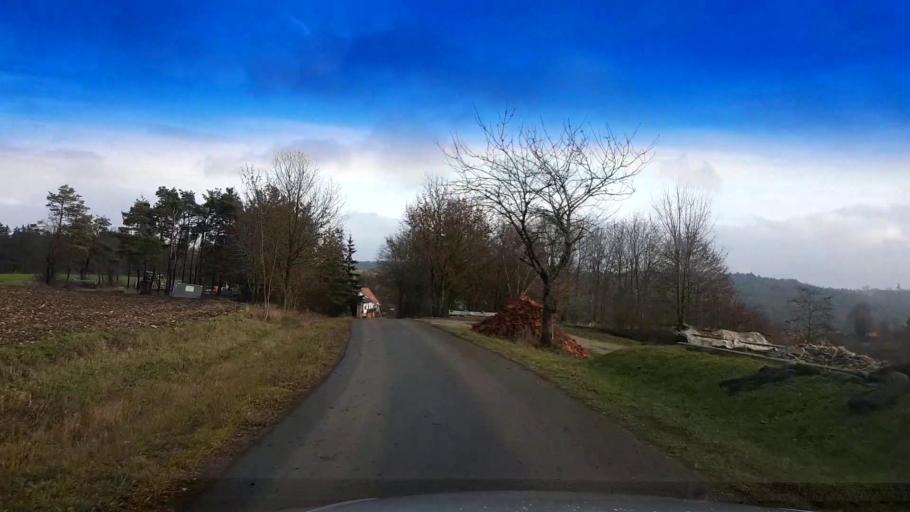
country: DE
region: Bavaria
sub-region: Upper Franconia
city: Poxdorf
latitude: 49.9231
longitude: 11.1224
